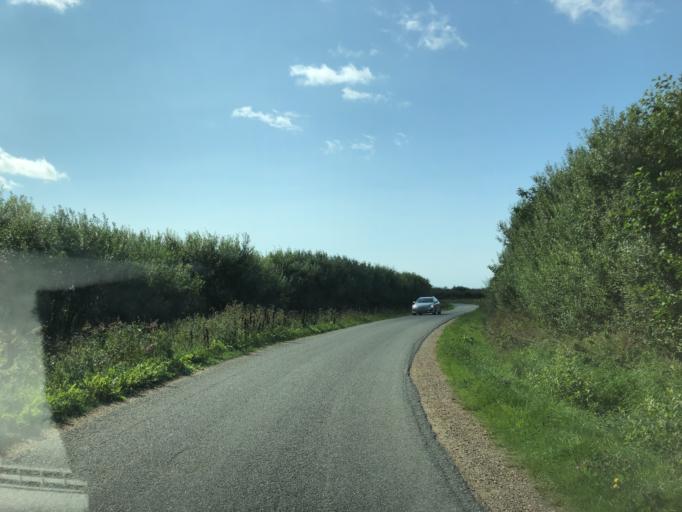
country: DK
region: Central Jutland
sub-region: Holstebro Kommune
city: Ulfborg
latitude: 56.2591
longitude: 8.1592
